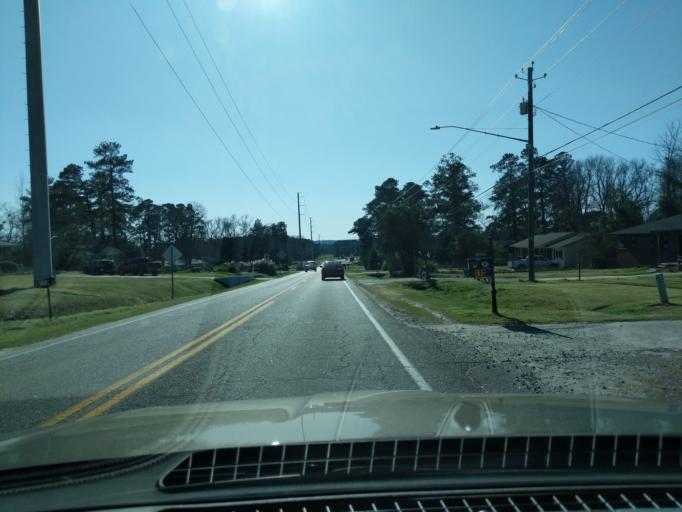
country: US
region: Georgia
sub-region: Columbia County
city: Grovetown
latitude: 33.4536
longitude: -82.2090
